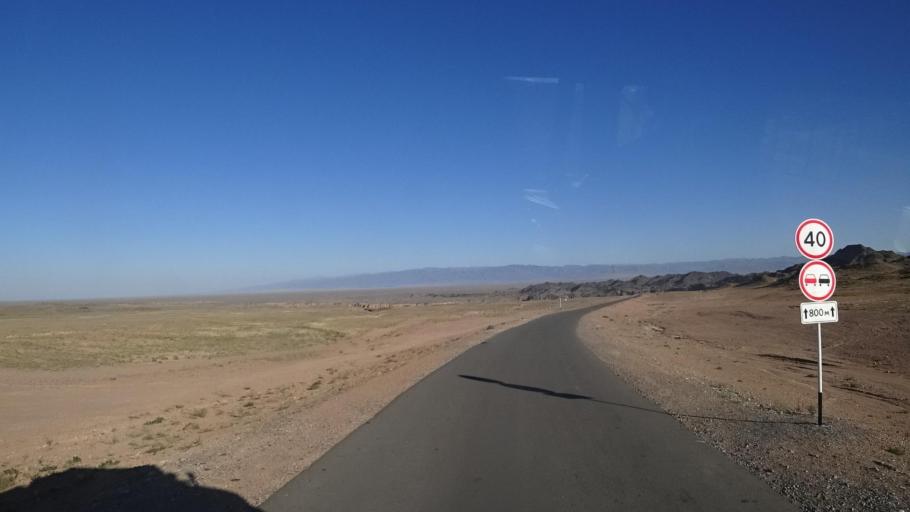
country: KZ
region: Almaty Oblysy
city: Kegen
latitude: 43.3614
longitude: 79.0477
